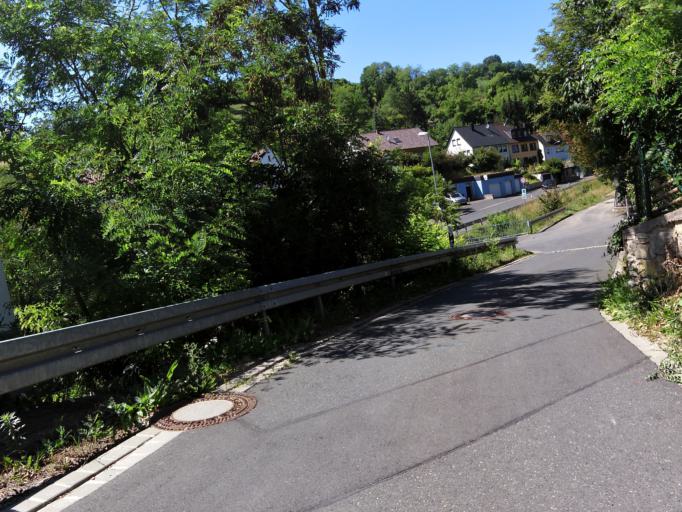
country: DE
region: Bavaria
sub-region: Regierungsbezirk Unterfranken
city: Randersacker
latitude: 49.7626
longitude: 9.9902
